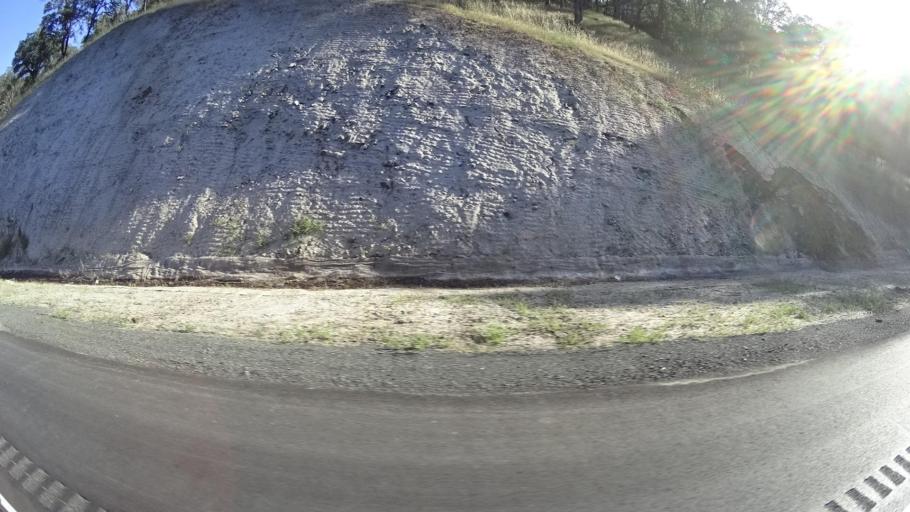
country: US
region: California
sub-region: Lake County
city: Upper Lake
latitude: 39.1649
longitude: -122.9673
